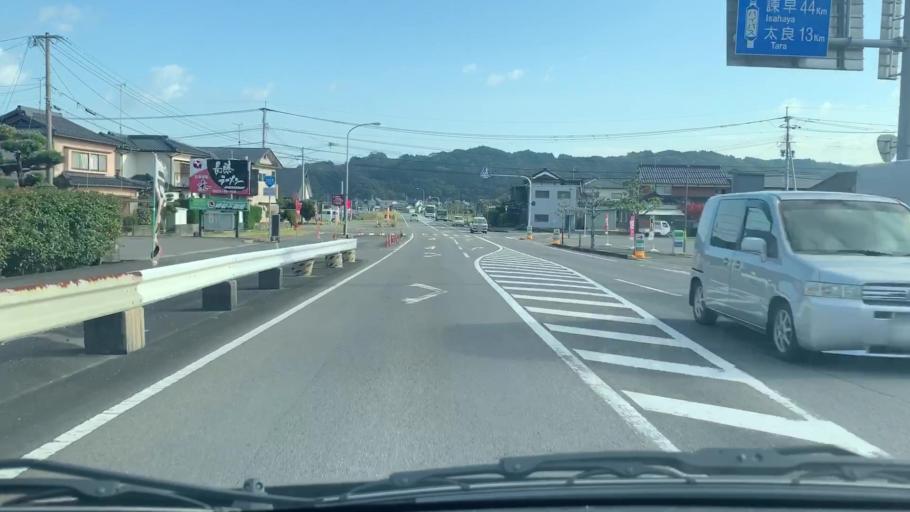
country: JP
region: Saga Prefecture
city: Kashima
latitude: 33.0940
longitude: 130.0941
